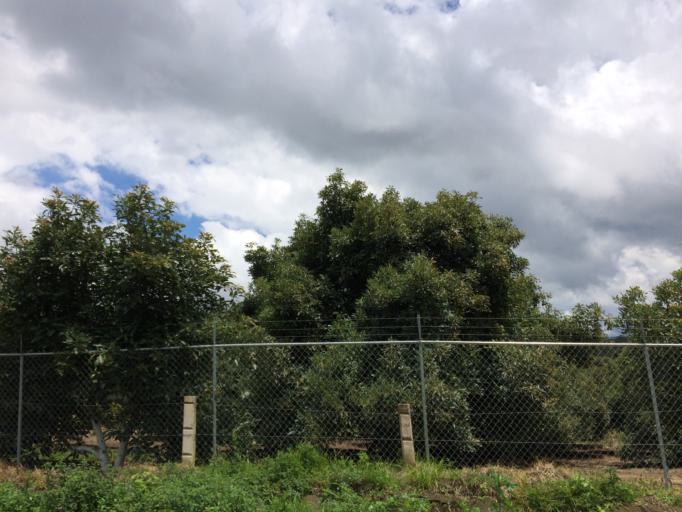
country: MX
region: Michoacan
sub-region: Uruapan
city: Santa Ana Zirosto
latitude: 19.5534
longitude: -102.3107
